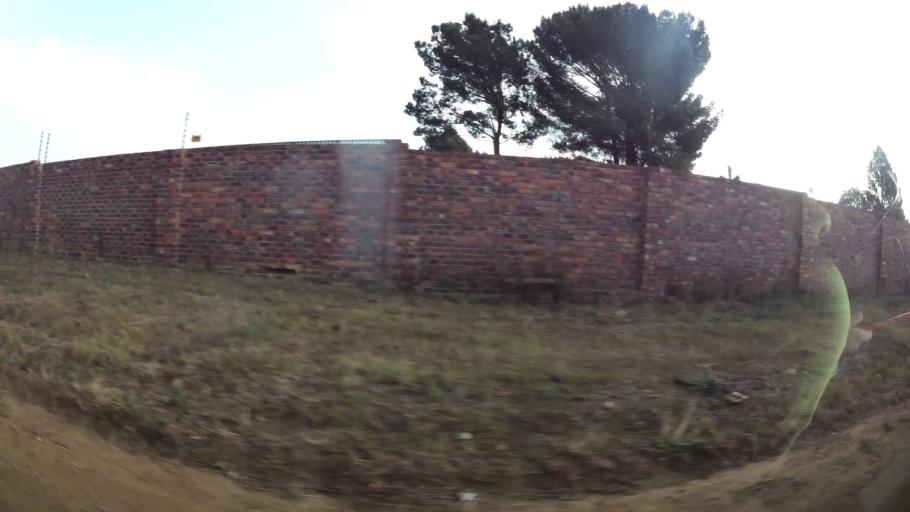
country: ZA
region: Gauteng
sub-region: Ekurhuleni Metropolitan Municipality
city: Benoni
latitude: -26.1071
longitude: 28.2847
